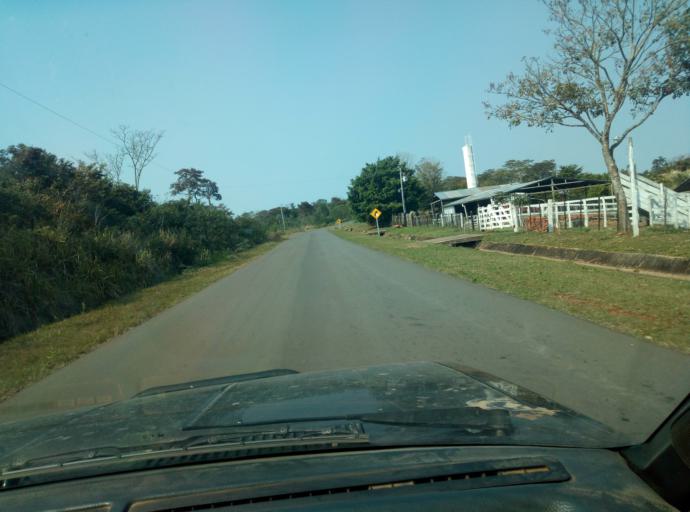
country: PY
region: Caaguazu
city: Carayao
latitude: -25.2013
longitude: -56.3078
